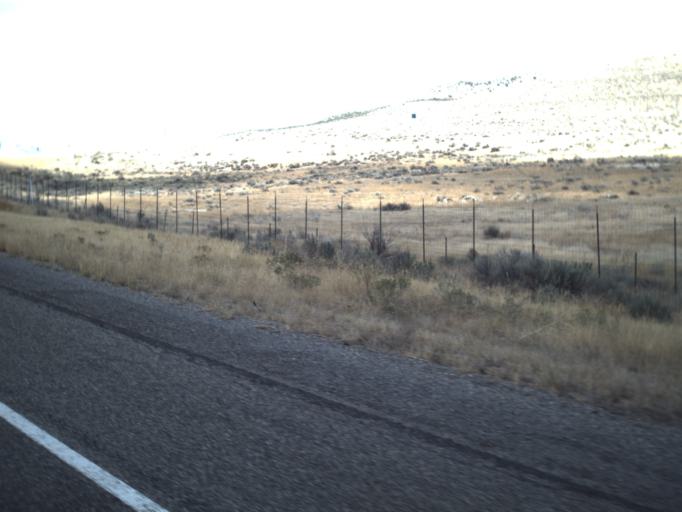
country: US
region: Idaho
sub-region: Oneida County
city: Malad City
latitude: 41.9625
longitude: -112.7495
